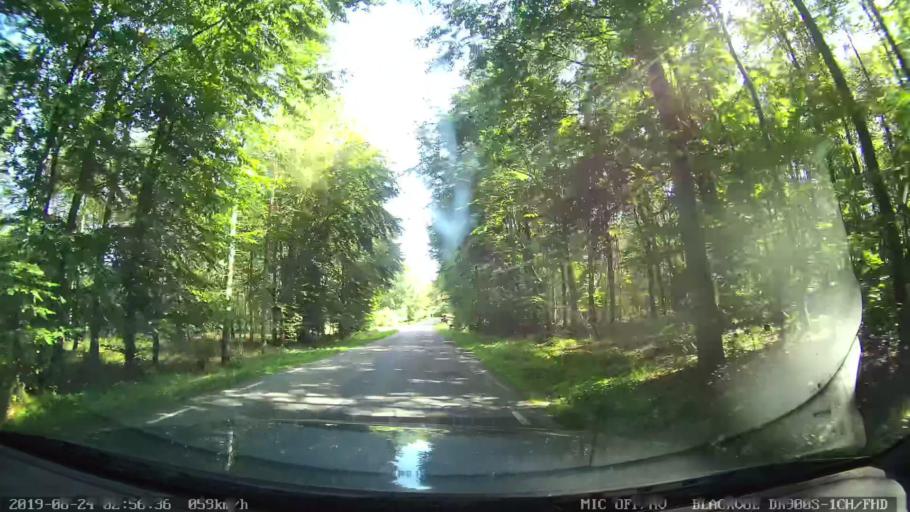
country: SE
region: Skane
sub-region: Trelleborgs Kommun
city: Anderslov
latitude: 55.4884
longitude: 13.3962
